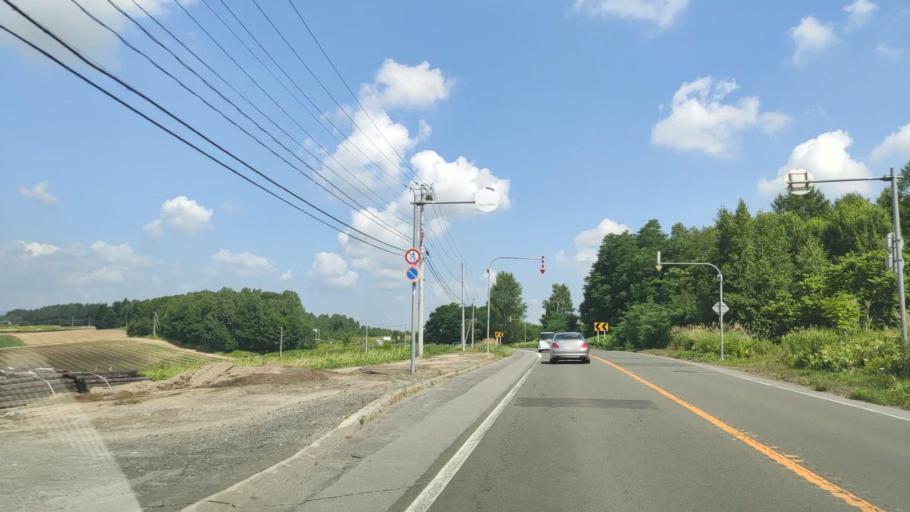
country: JP
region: Hokkaido
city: Shimo-furano
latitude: 43.5045
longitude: 142.4588
